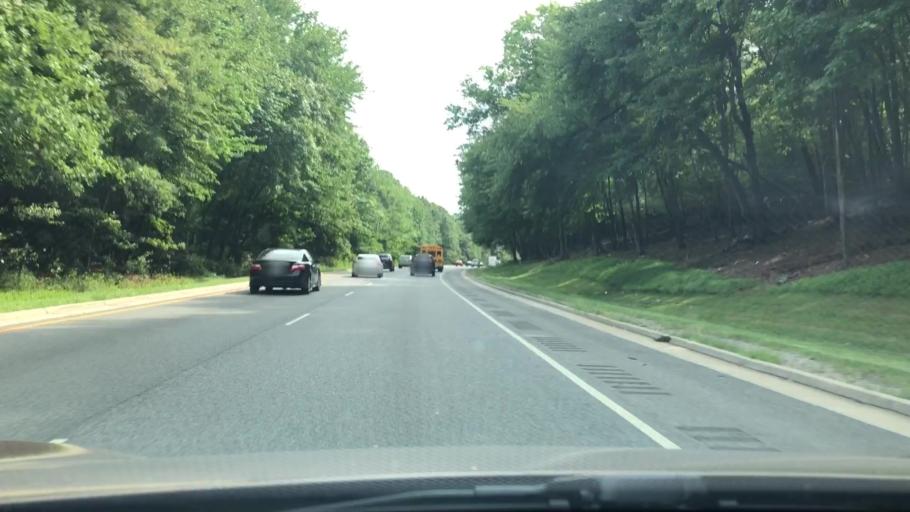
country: US
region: Maryland
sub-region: Prince George's County
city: New Carrollton
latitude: 38.9807
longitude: -76.8938
